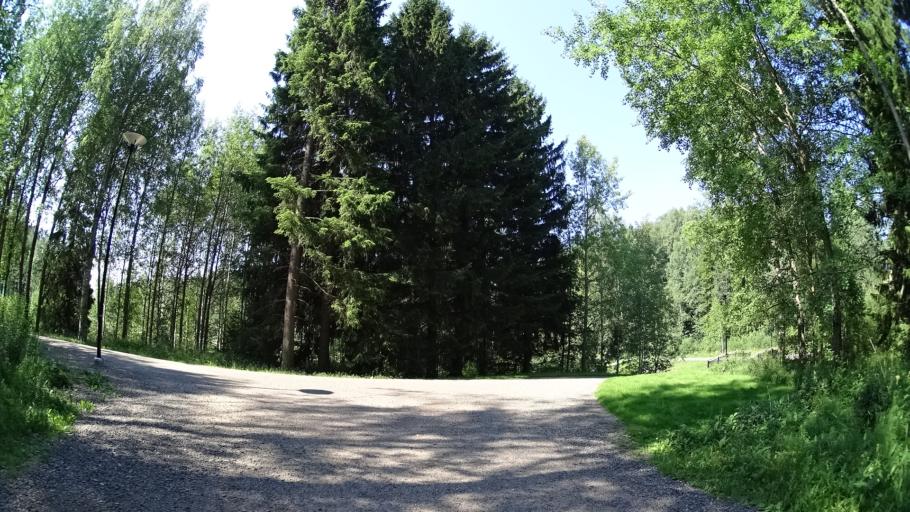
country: FI
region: Uusimaa
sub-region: Helsinki
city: Kerava
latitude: 60.3568
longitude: 25.0746
